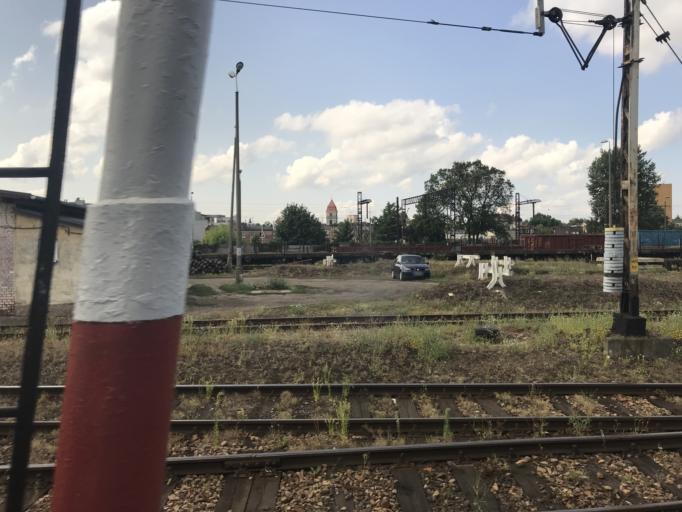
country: PL
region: Kujawsko-Pomorskie
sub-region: Bydgoszcz
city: Bydgoszcz
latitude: 53.1323
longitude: 17.9788
